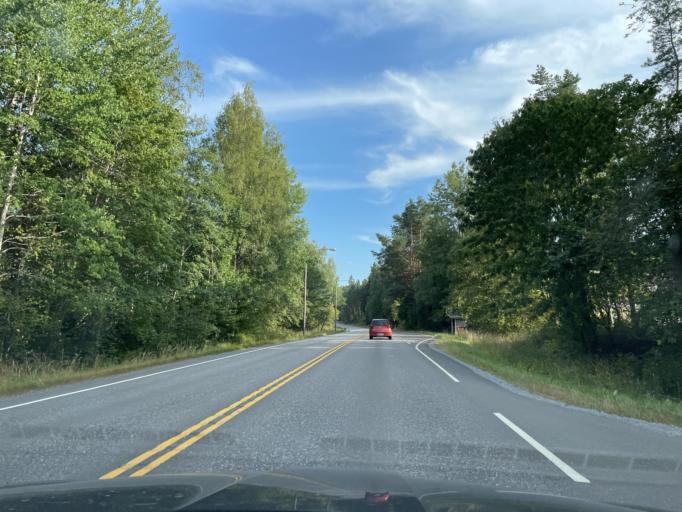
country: FI
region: Paijanne Tavastia
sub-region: Lahti
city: Padasjoki
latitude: 61.3850
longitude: 25.1899
